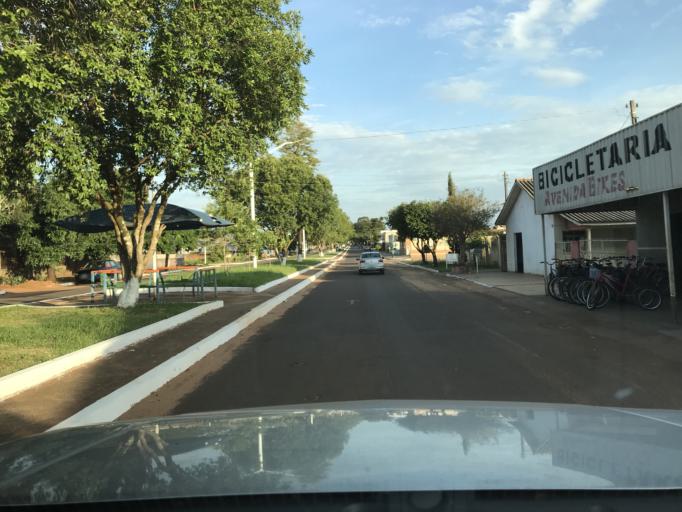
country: BR
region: Mato Grosso do Sul
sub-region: Iguatemi
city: Iguatemi
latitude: -23.6673
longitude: -54.5620
